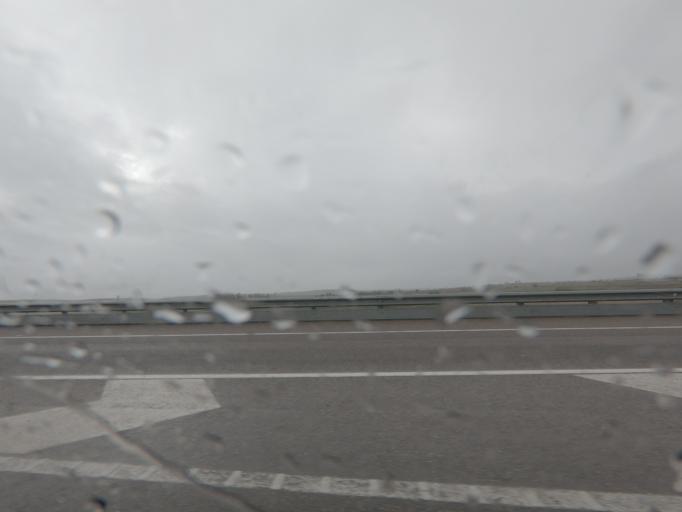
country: ES
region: Extremadura
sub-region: Provincia de Badajoz
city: Badajoz
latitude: 38.9151
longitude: -6.9632
